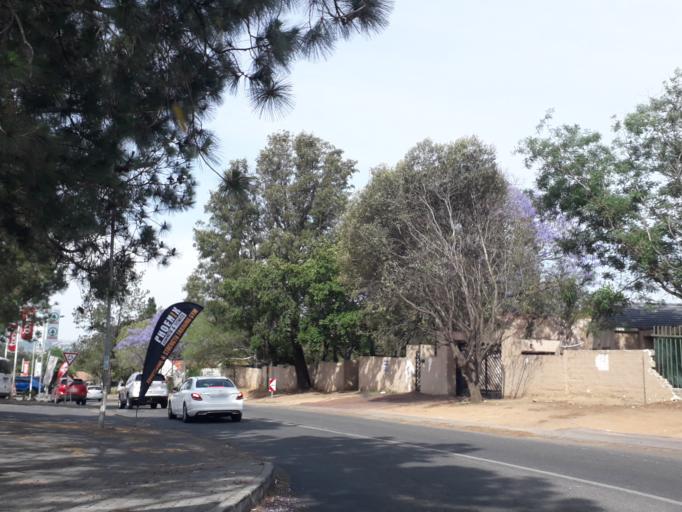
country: ZA
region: Gauteng
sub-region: City of Johannesburg Metropolitan Municipality
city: Roodepoort
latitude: -26.0786
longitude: 27.9459
